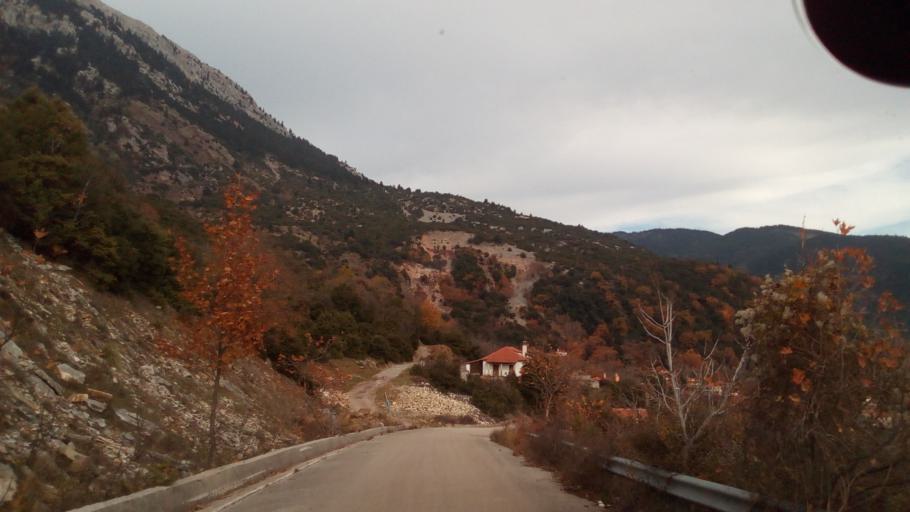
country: GR
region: West Greece
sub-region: Nomos Aitolias kai Akarnanias
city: Thermo
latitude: 38.6760
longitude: 21.8951
